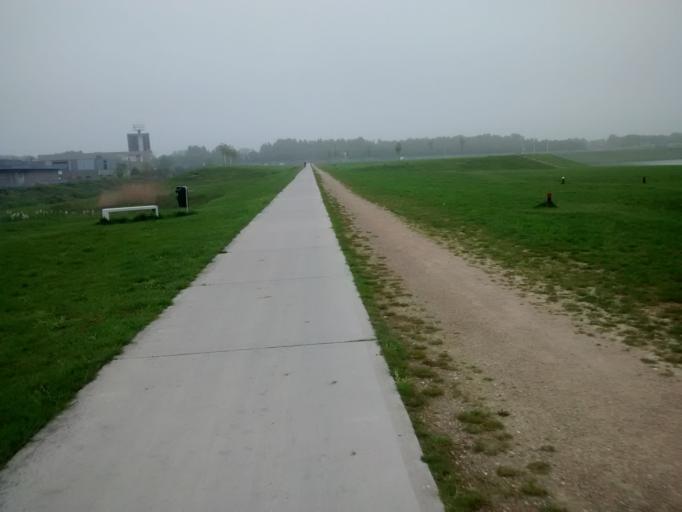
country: NL
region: Utrecht
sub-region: Gemeente Utrecht
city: Lunetten
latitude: 52.0513
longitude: 5.1251
